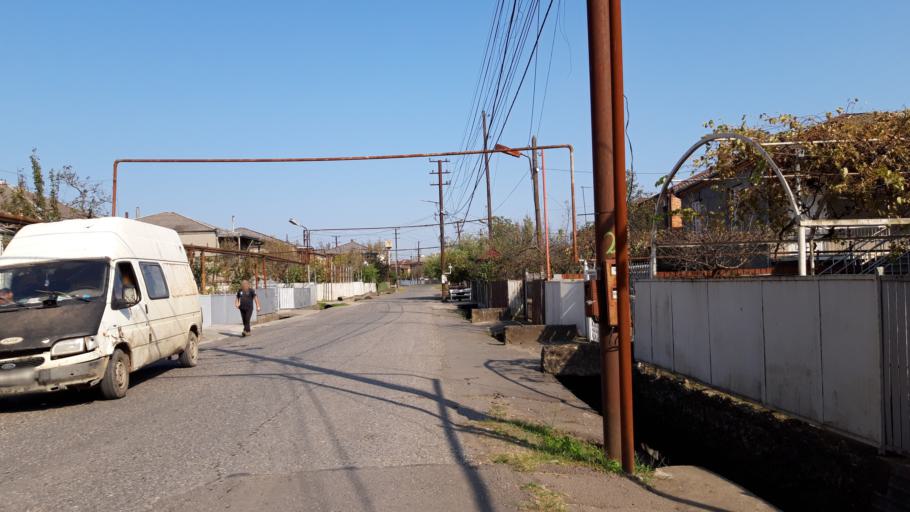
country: GE
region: Imereti
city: Samtredia
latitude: 42.1607
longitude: 42.3342
